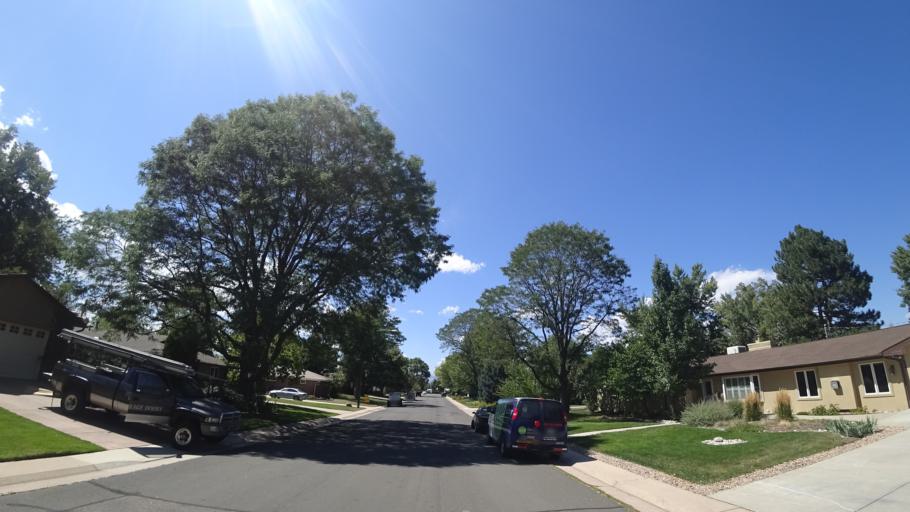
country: US
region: Colorado
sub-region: Arapahoe County
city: Greenwood Village
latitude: 39.6052
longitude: -104.9761
